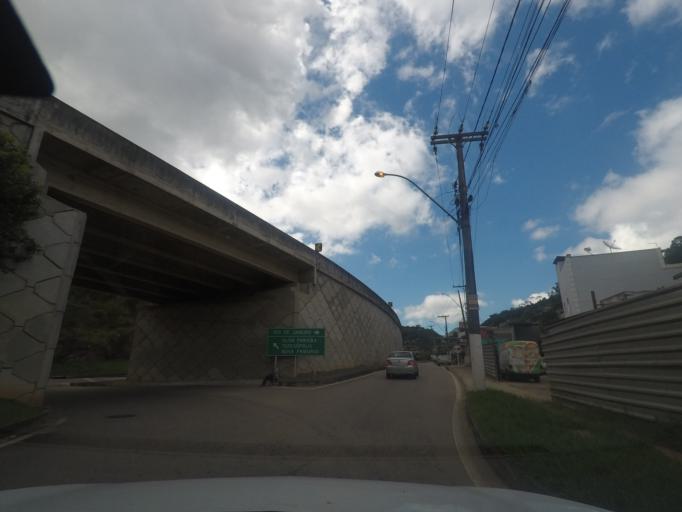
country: BR
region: Rio de Janeiro
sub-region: Teresopolis
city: Teresopolis
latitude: -22.3893
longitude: -42.9535
